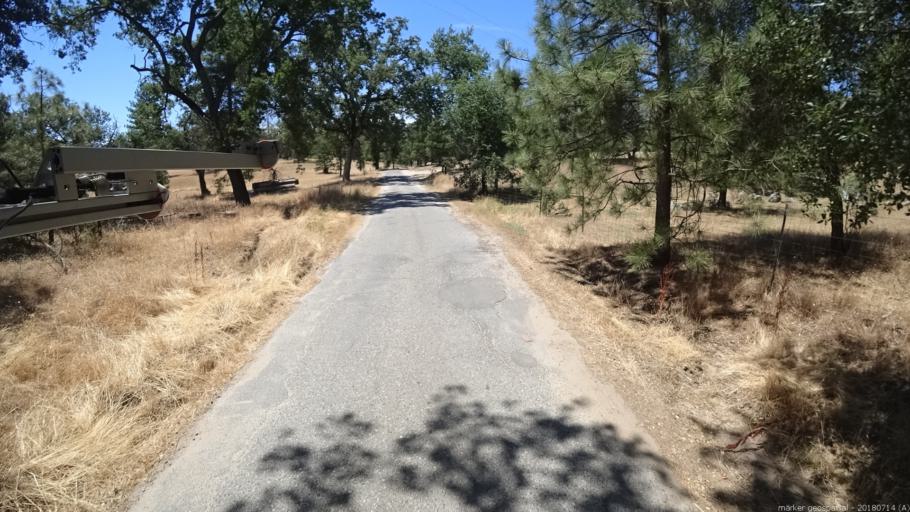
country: US
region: California
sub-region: Madera County
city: Ahwahnee
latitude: 37.3961
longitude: -119.7408
